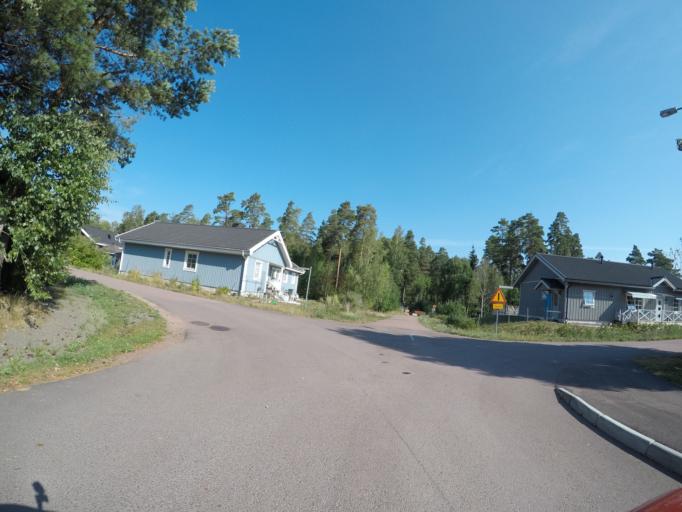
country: AX
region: Alands landsbygd
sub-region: Finstroem
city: Finstroem
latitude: 60.2284
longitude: 19.9784
